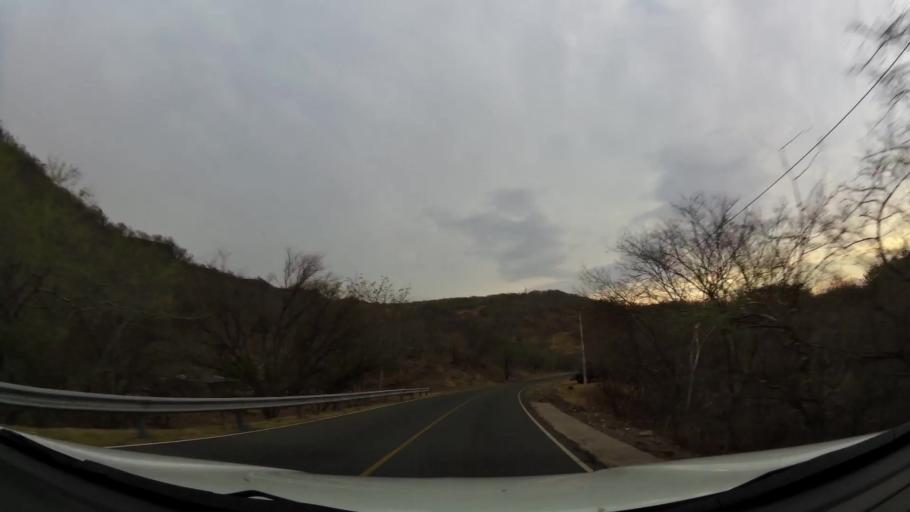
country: NI
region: Leon
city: La Jicaral
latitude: 12.6798
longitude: -86.4270
